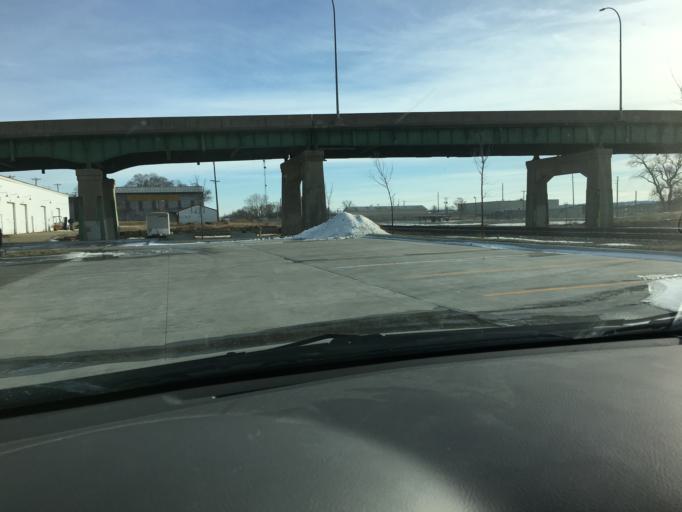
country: US
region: Iowa
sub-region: Wapello County
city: Ottumwa
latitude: 41.0151
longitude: -92.4104
